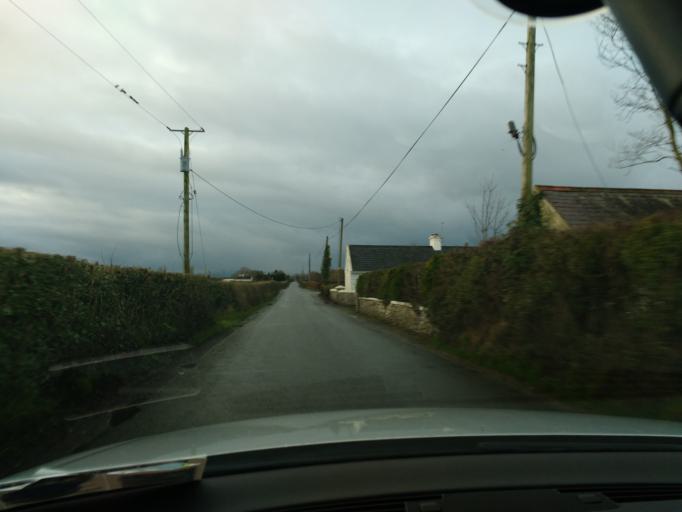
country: IE
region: Munster
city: Thurles
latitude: 52.6359
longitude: -7.8382
